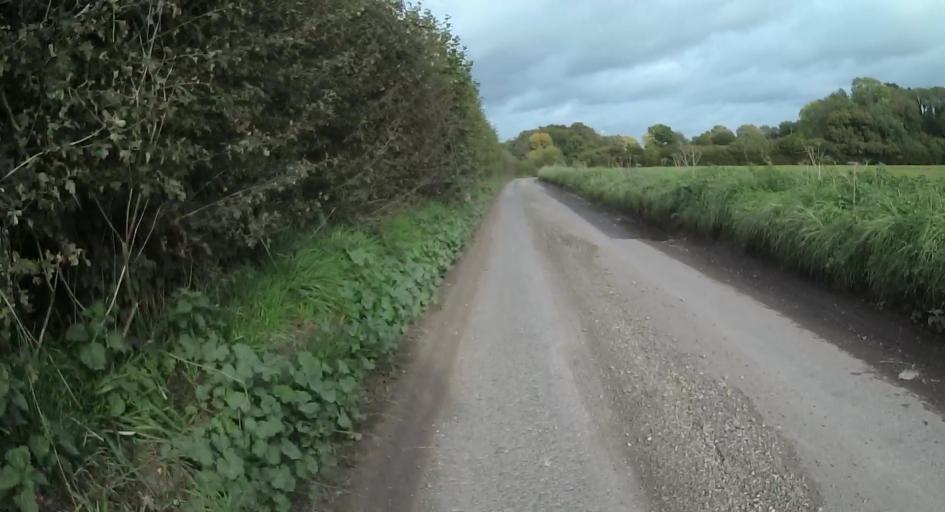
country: GB
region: England
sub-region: Hampshire
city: Long Sutton
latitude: 51.1670
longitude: -0.9269
